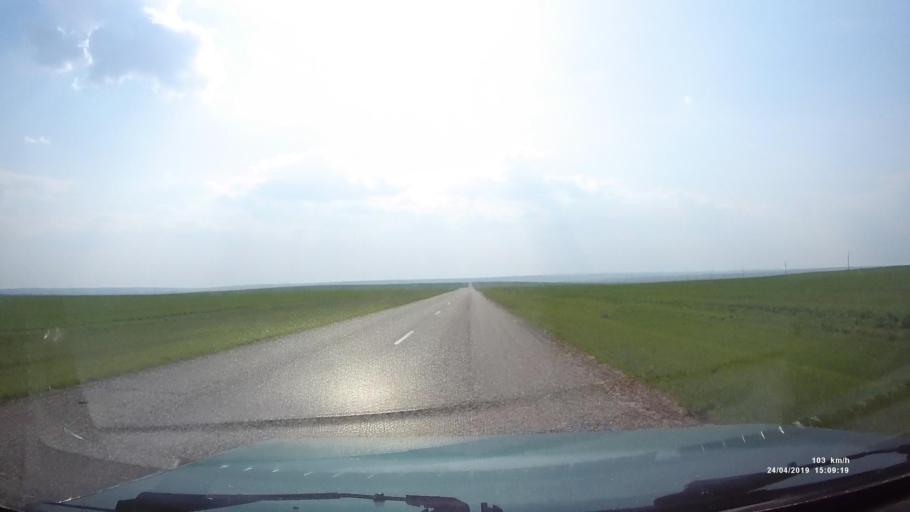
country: RU
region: Rostov
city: Remontnoye
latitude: 46.5560
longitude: 43.3643
